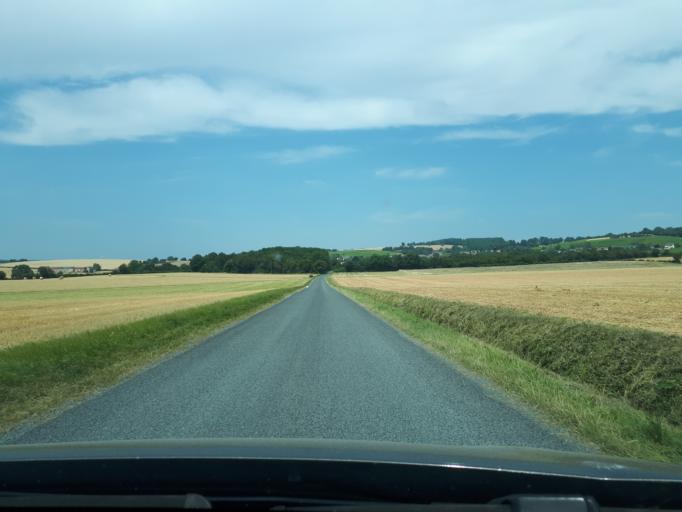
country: FR
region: Centre
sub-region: Departement du Cher
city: Sancerre
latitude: 47.2940
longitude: 2.7529
